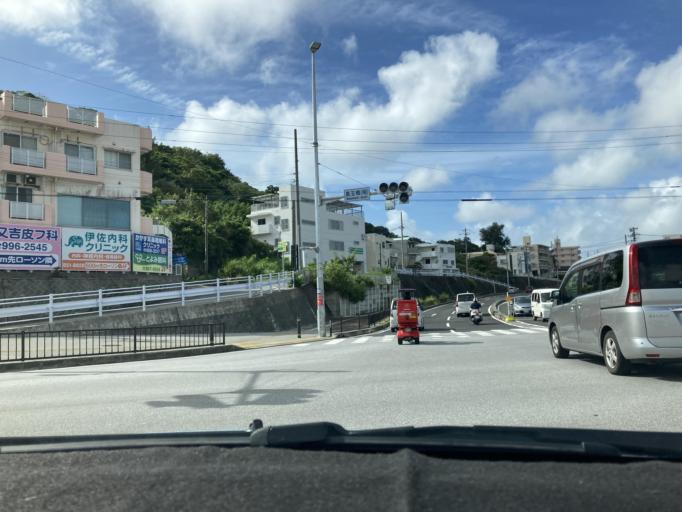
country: JP
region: Okinawa
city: Tomigusuku
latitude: 26.1937
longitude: 127.6953
